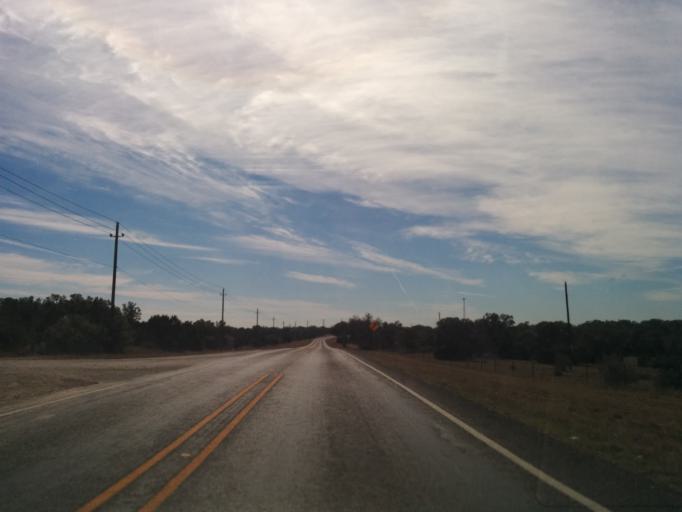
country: US
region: Texas
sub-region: Bexar County
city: Fair Oaks Ranch
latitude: 29.8762
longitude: -98.5590
